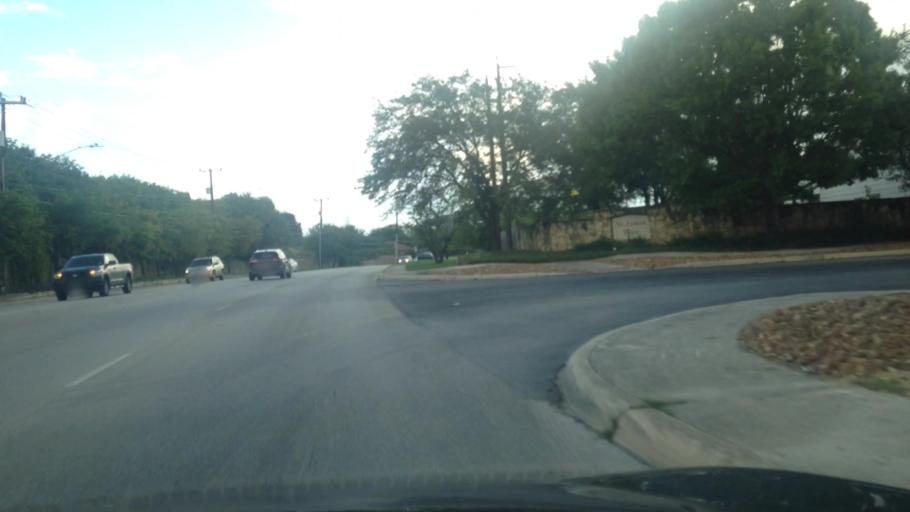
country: US
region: Texas
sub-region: Bexar County
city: Windcrest
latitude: 29.5692
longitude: -98.4196
